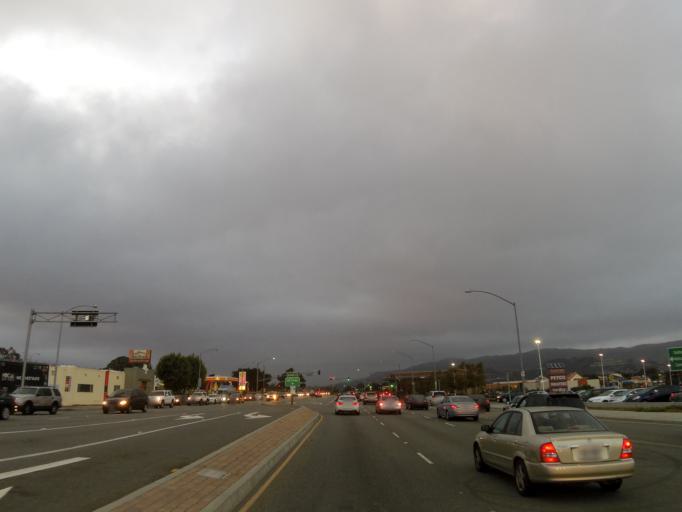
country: US
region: California
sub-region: San Mateo County
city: San Bruno
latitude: 37.6354
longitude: -122.4204
